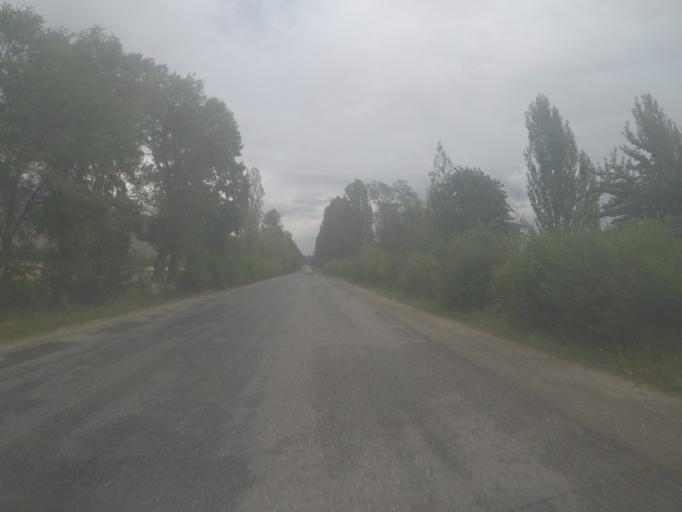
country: KG
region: Ysyk-Koel
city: Tyup
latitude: 42.7374
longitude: 77.9960
